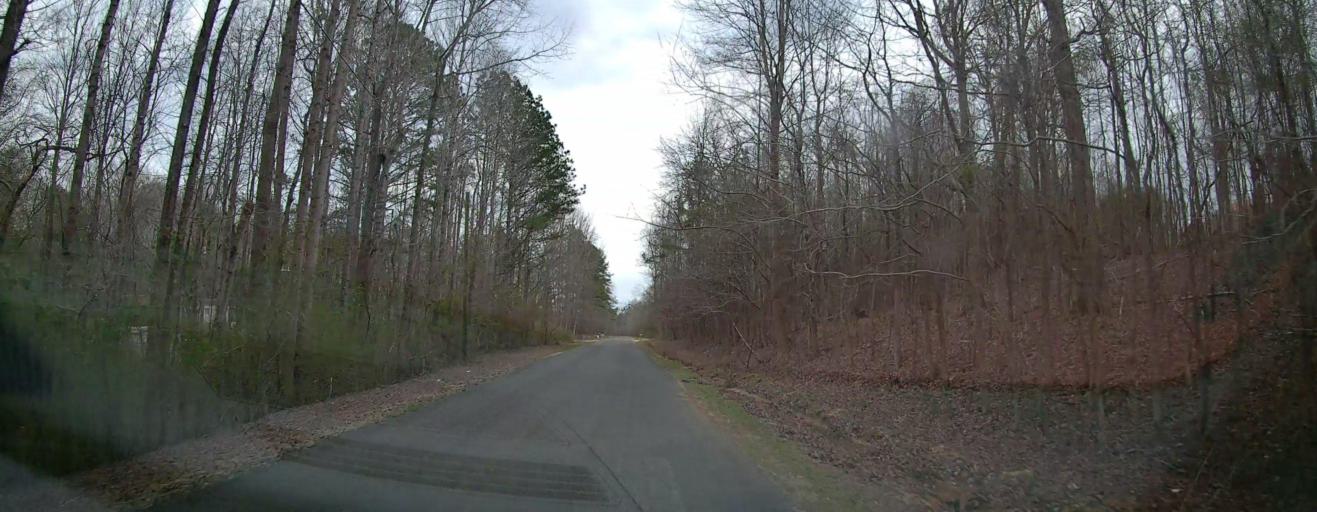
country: US
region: Alabama
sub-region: Marion County
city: Hamilton
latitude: 34.2024
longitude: -88.1899
